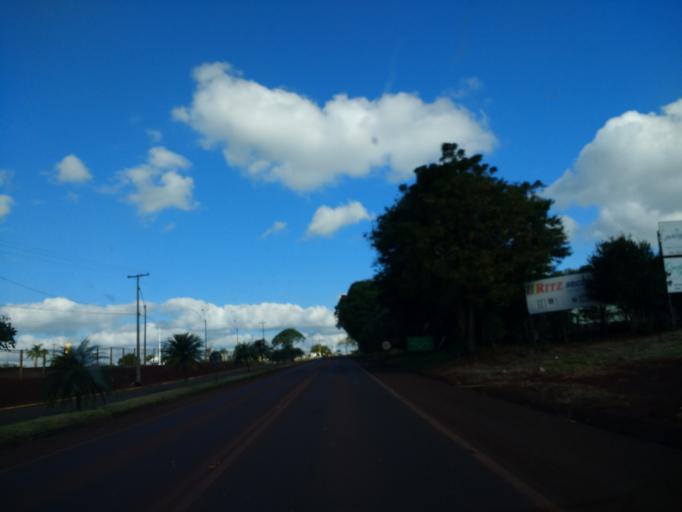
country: BR
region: Parana
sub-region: Palotina
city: Palotina
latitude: -24.4059
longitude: -53.5351
